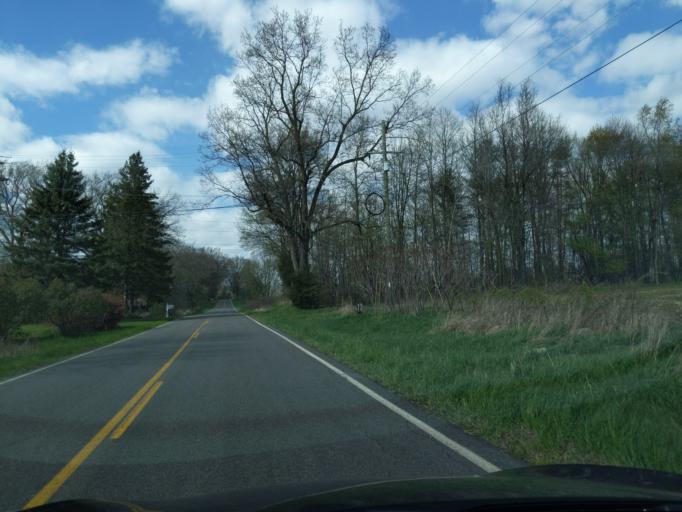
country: US
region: Michigan
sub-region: Ingham County
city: Leslie
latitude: 42.4149
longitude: -84.5415
